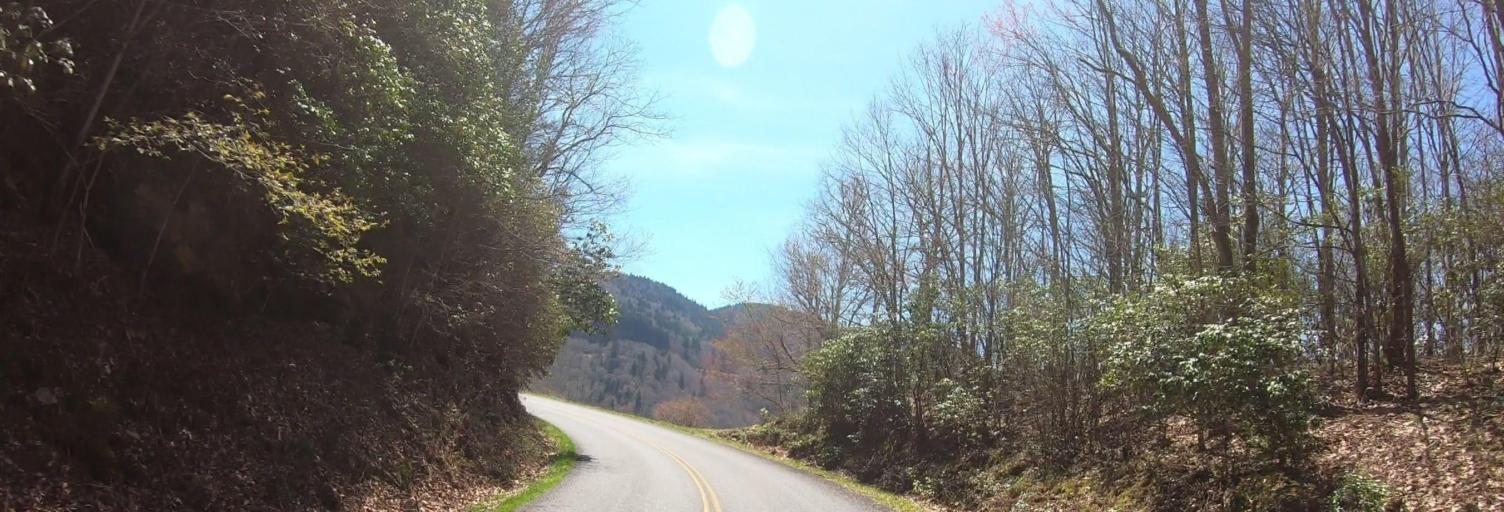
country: US
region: North Carolina
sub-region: Haywood County
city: Maggie Valley
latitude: 35.4790
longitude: -83.1489
